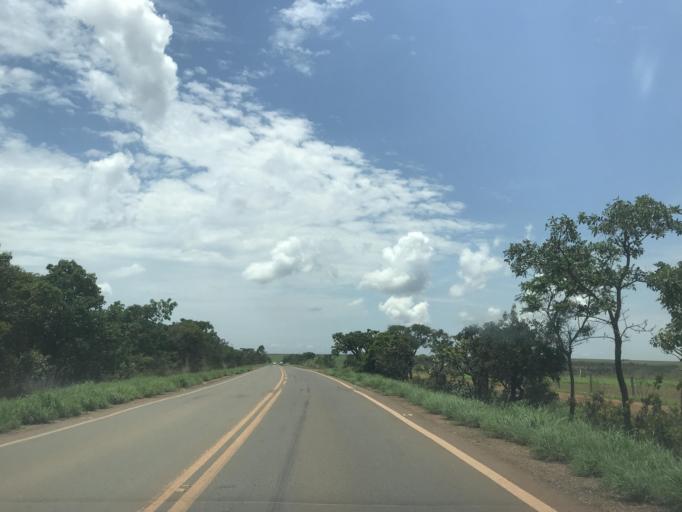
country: BR
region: Goias
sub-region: Luziania
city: Luziania
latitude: -16.4752
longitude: -48.2101
